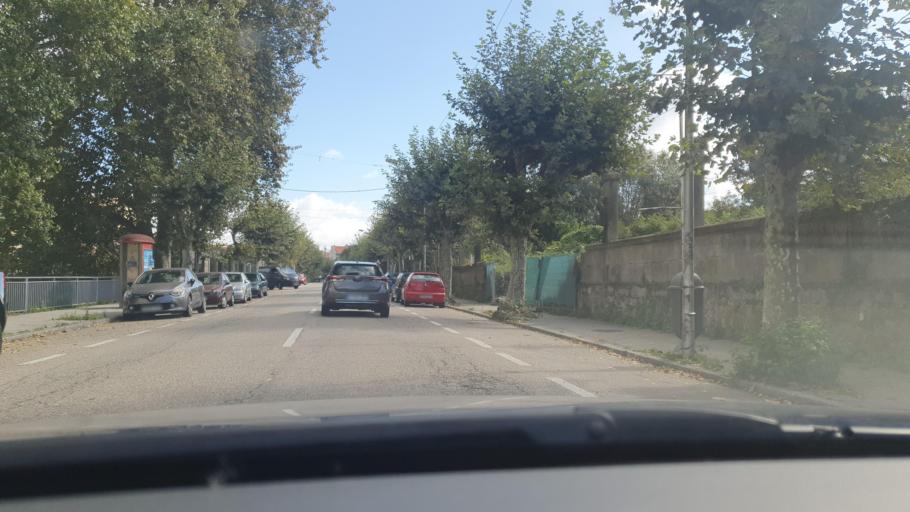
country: ES
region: Galicia
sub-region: Provincia de Pontevedra
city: Vigo
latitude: 42.2210
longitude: -8.7658
